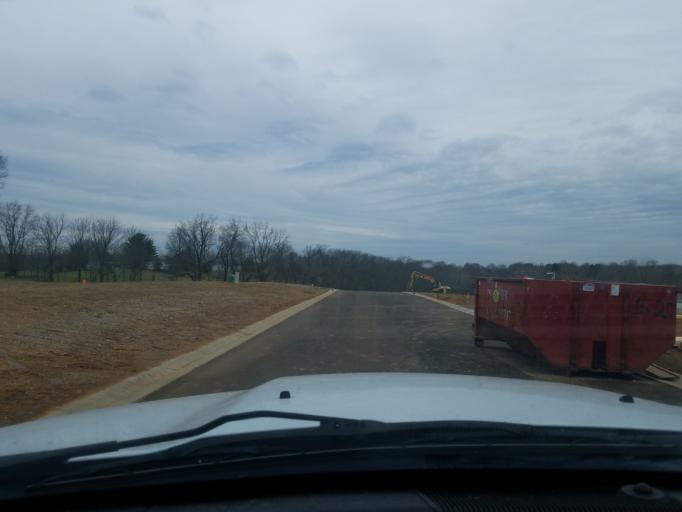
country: US
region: Kentucky
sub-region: Jefferson County
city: Prospect
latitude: 38.3380
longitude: -85.6601
